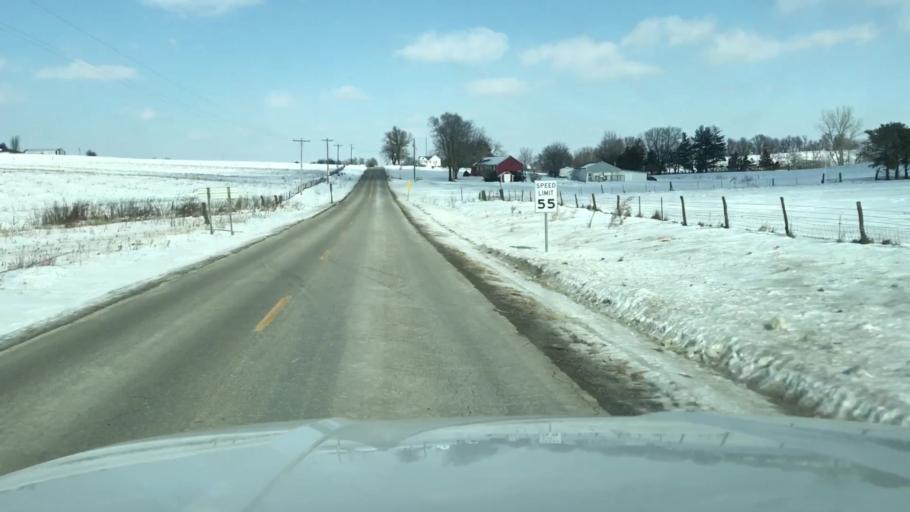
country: US
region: Missouri
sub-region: Nodaway County
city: Maryville
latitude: 40.3446
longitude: -94.7225
